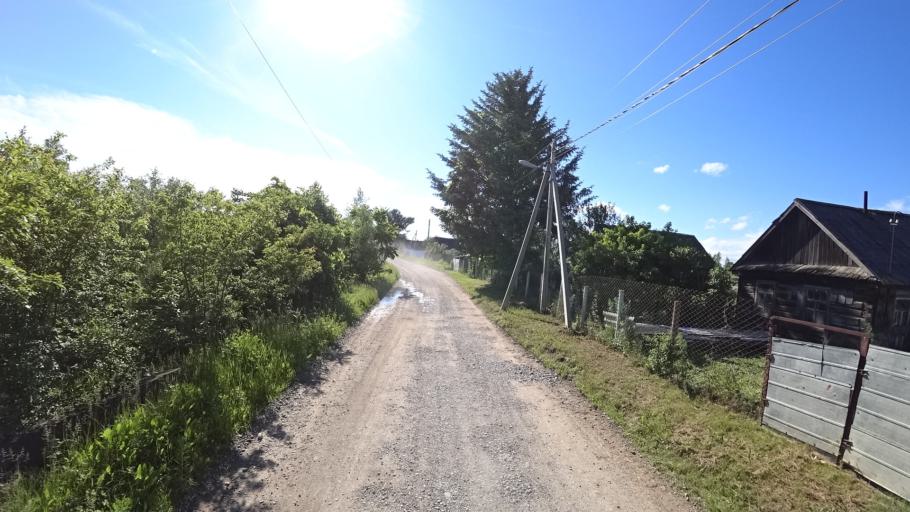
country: RU
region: Khabarovsk Krai
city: Khor
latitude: 47.8867
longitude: 135.0145
